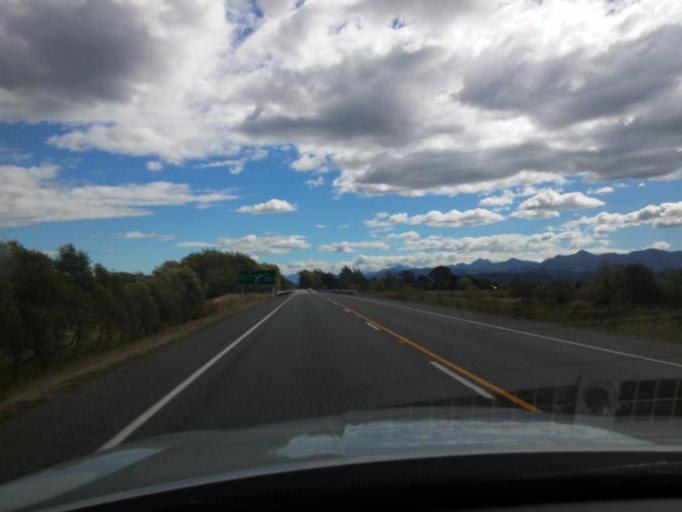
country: NZ
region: Marlborough
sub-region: Marlborough District
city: Blenheim
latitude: -41.5133
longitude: 173.8442
